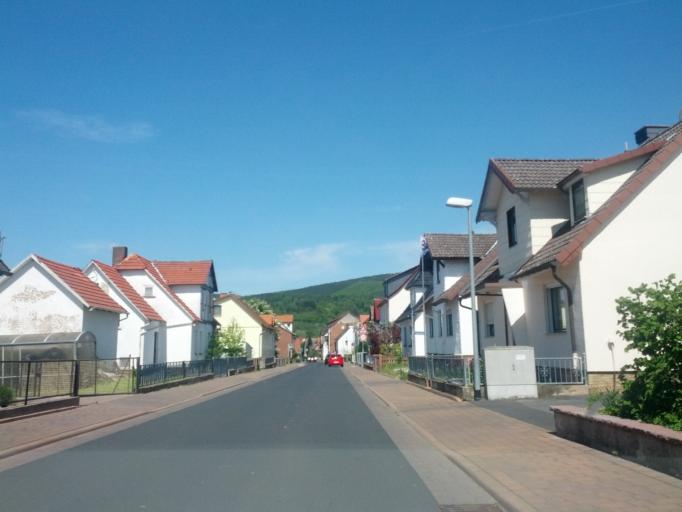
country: DE
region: Hesse
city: Witzenhausen
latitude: 51.3382
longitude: 9.8851
